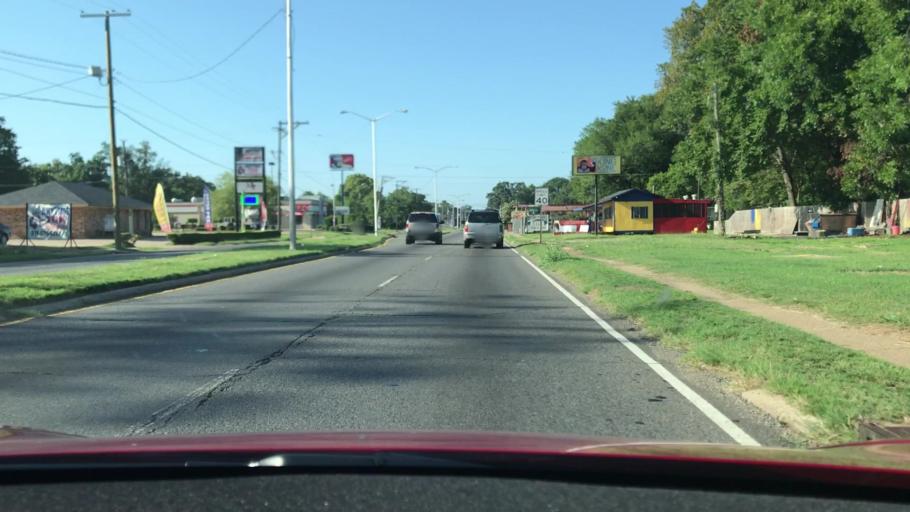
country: US
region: Louisiana
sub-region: Caddo Parish
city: Shreveport
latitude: 32.4763
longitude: -93.7801
